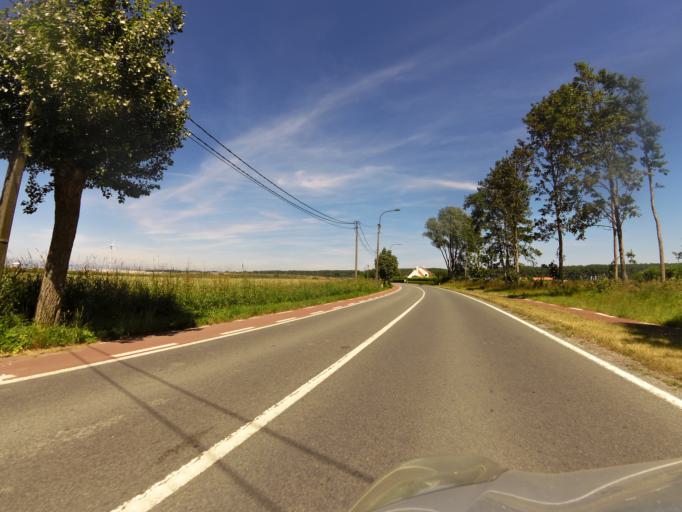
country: BE
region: Flanders
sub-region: Provincie West-Vlaanderen
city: Damme
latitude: 51.2889
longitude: 3.2533
